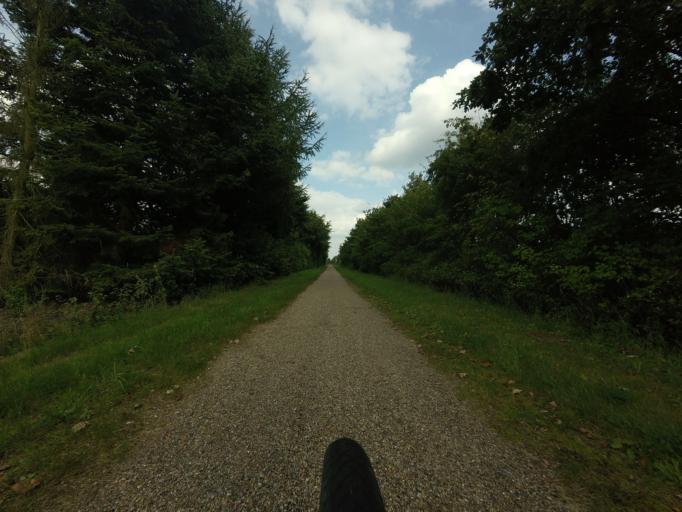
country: DK
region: Central Jutland
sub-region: Herning Kommune
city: Sunds
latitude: 56.2268
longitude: 9.0722
